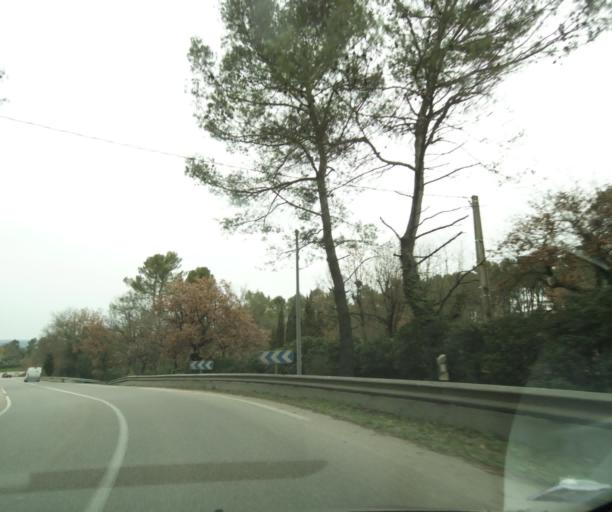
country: FR
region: Provence-Alpes-Cote d'Azur
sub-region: Departement des Bouches-du-Rhone
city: Fuveau
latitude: 43.4610
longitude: 5.5473
